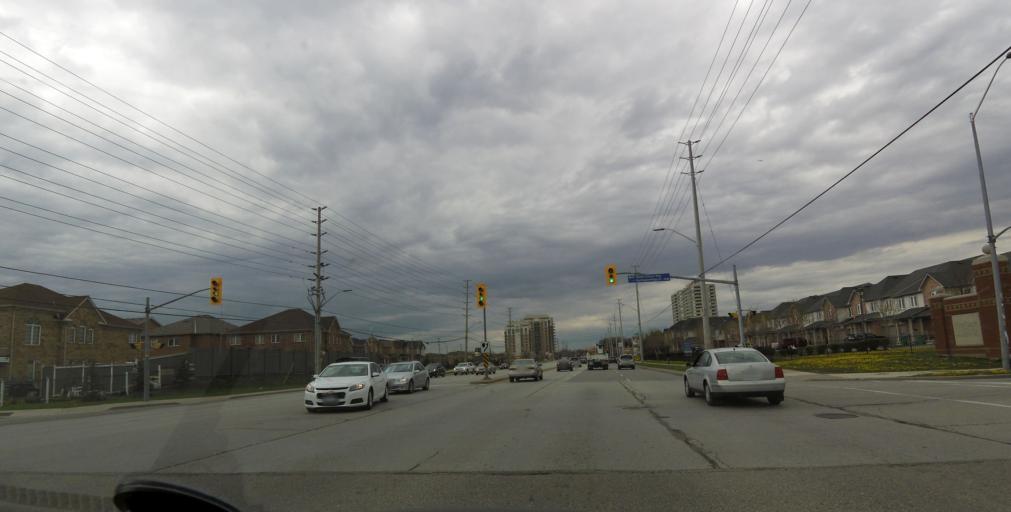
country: CA
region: Ontario
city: Mississauga
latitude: 43.5902
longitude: -79.6661
